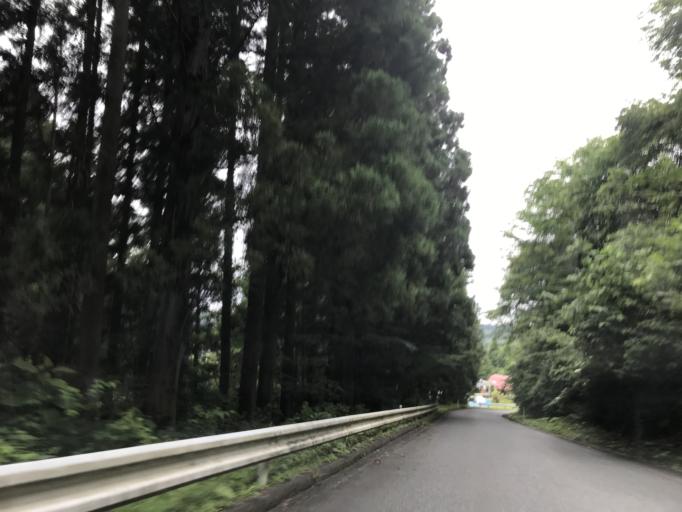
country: JP
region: Iwate
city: Ichinoseki
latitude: 38.8290
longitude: 141.2354
